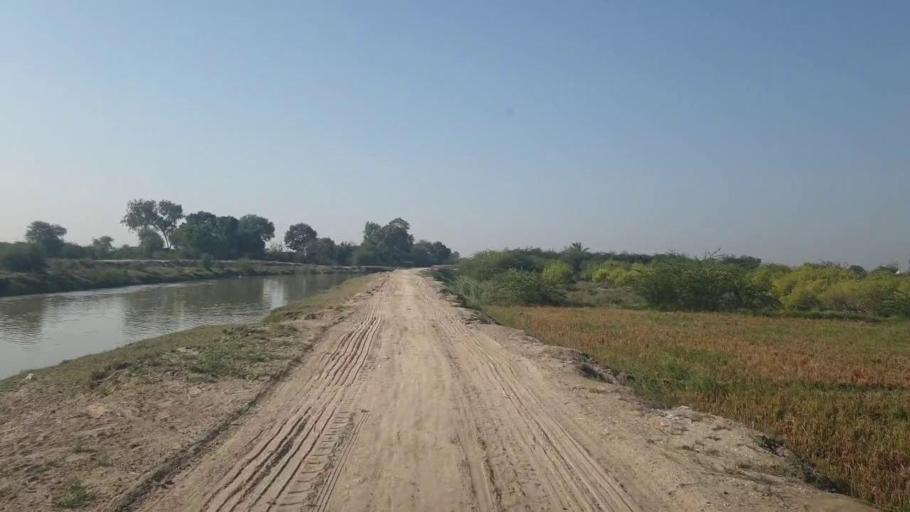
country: PK
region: Sindh
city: Badin
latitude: 24.6806
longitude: 68.8575
